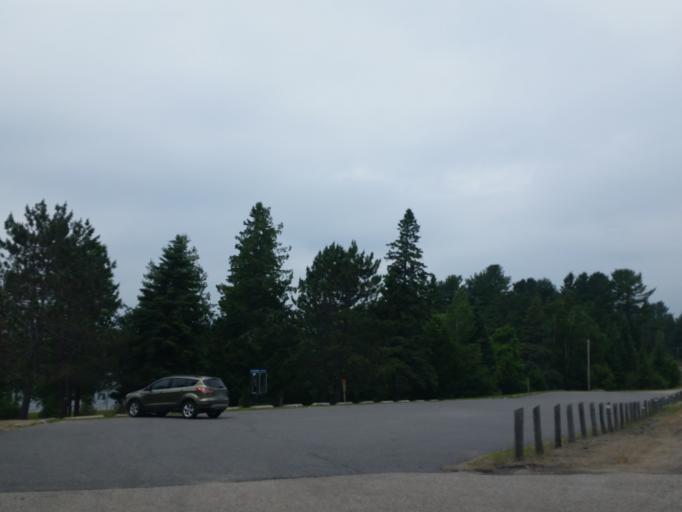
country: CA
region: Ontario
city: Mattawa
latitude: 45.5855
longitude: -78.4778
